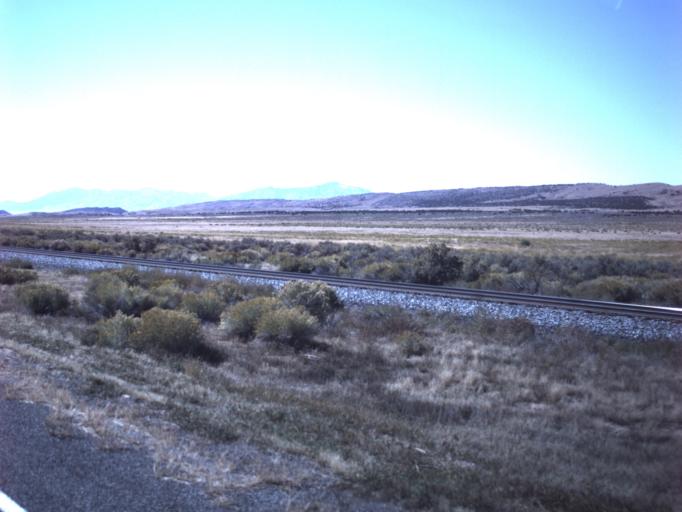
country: US
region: Utah
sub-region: Juab County
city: Nephi
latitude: 39.5317
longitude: -111.9323
